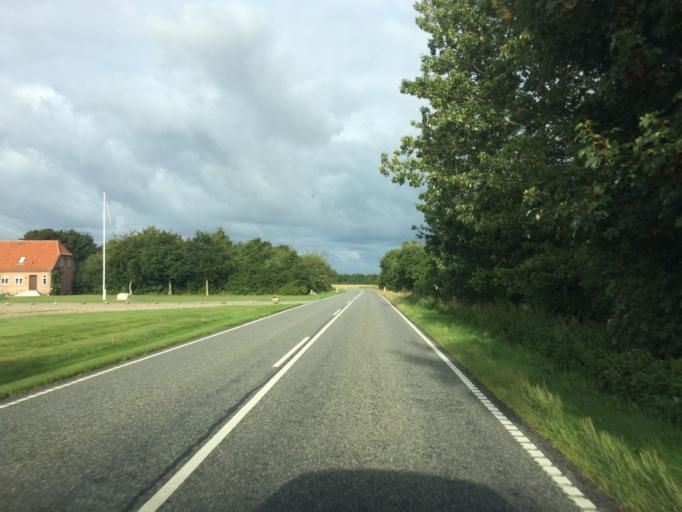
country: DK
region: Central Jutland
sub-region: Holstebro Kommune
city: Ulfborg
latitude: 56.1973
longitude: 8.3683
